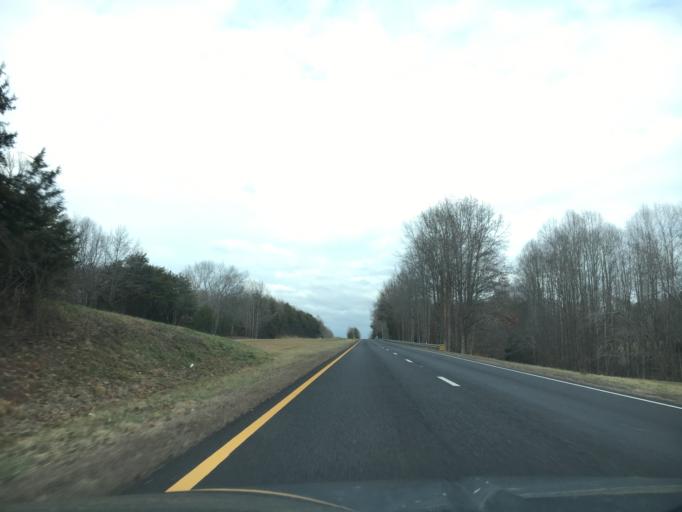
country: US
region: Virginia
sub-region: Lunenburg County
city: Victoria
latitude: 37.1156
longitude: -78.3440
